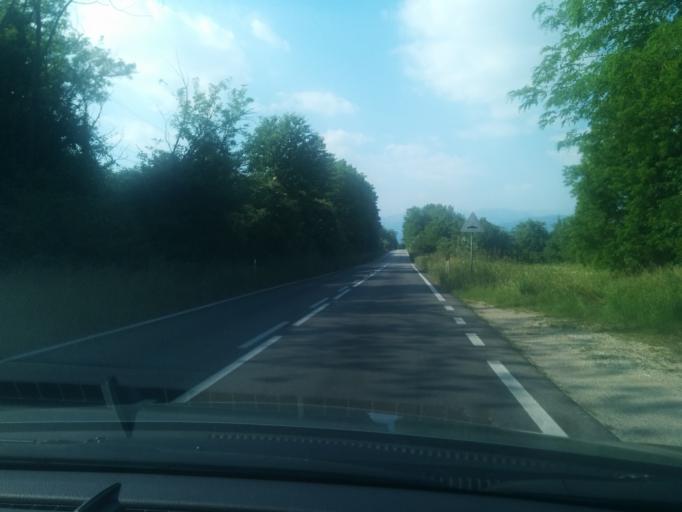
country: IT
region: Friuli Venezia Giulia
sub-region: Provincia di Udine
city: Reana del Rojale
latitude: 46.1338
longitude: 13.2442
